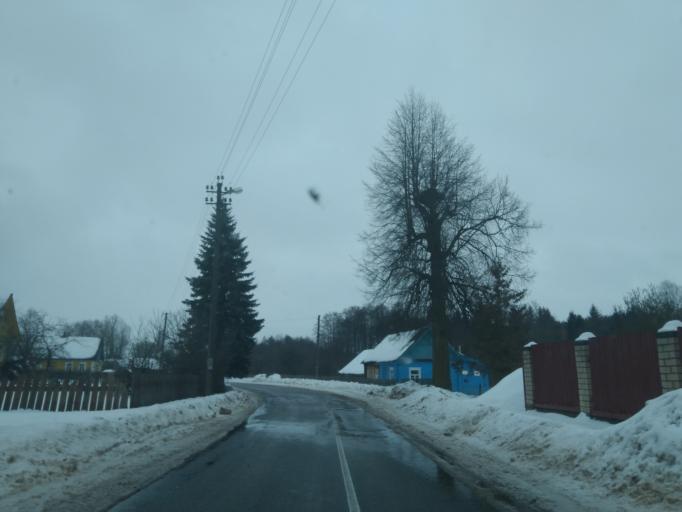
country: BY
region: Minsk
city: Ivyanyets
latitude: 53.8324
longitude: 26.8006
